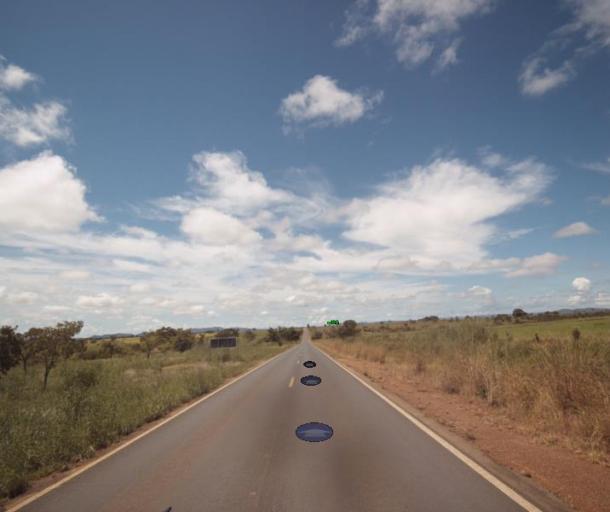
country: BR
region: Goias
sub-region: Padre Bernardo
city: Padre Bernardo
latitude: -15.2843
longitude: -48.2536
